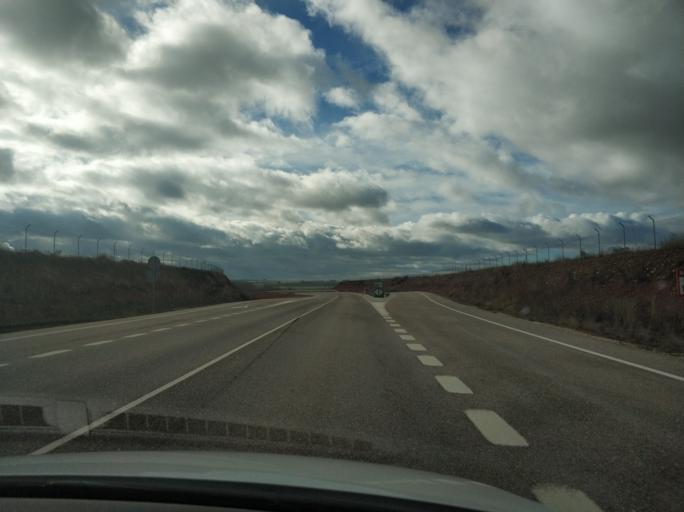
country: ES
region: Castille and Leon
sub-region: Provincia de Segovia
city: Ayllon
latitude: 41.4190
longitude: -3.4036
